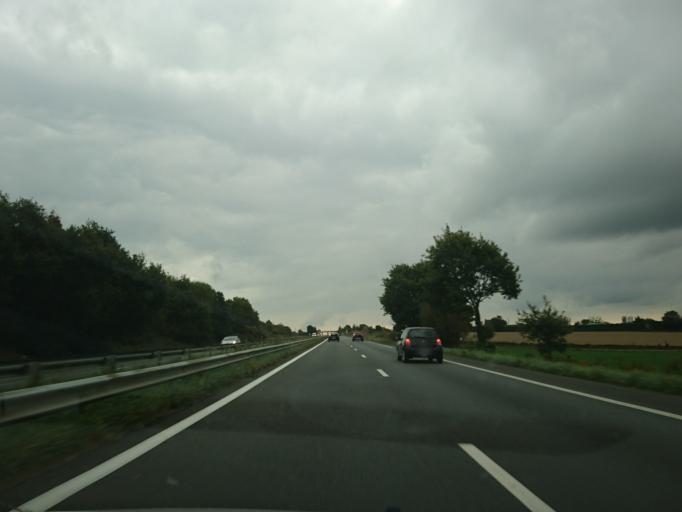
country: FR
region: Brittany
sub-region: Departement des Cotes-d'Armor
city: Sevignac
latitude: 48.3593
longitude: -2.3164
